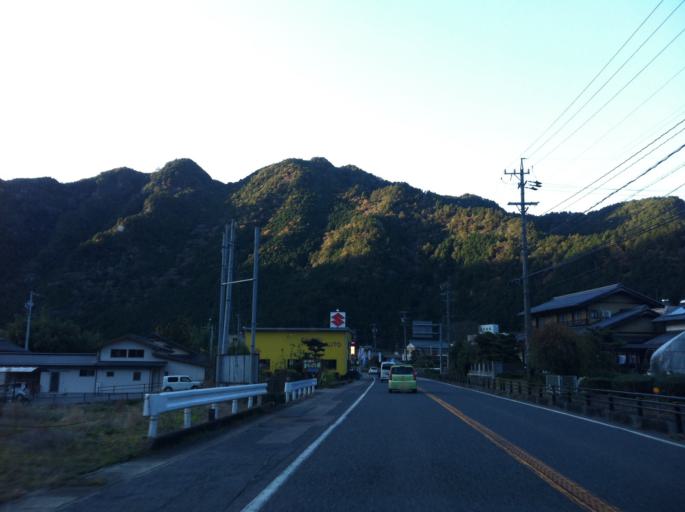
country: JP
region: Gifu
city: Mitake
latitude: 35.6010
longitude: 137.1669
